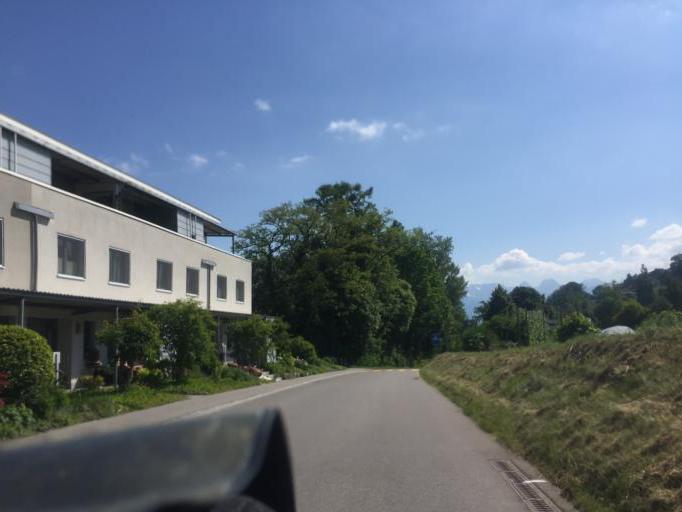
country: CH
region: Bern
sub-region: Bern-Mittelland District
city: Munsingen
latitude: 46.8441
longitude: 7.5448
